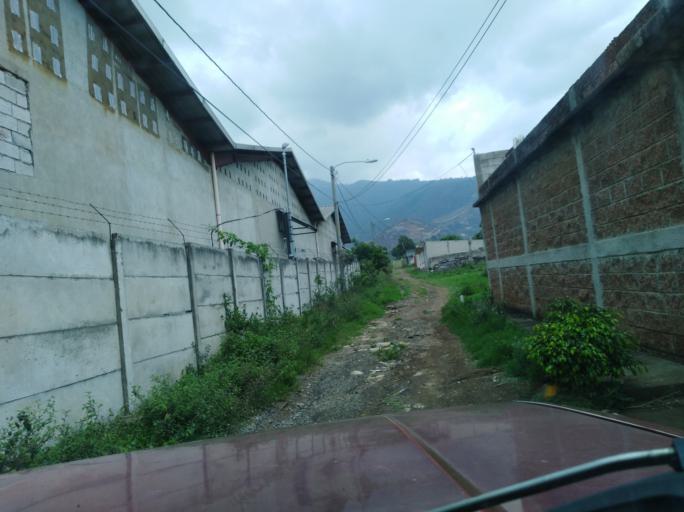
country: GT
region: Guatemala
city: Amatitlan
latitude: 14.5222
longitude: -90.6234
